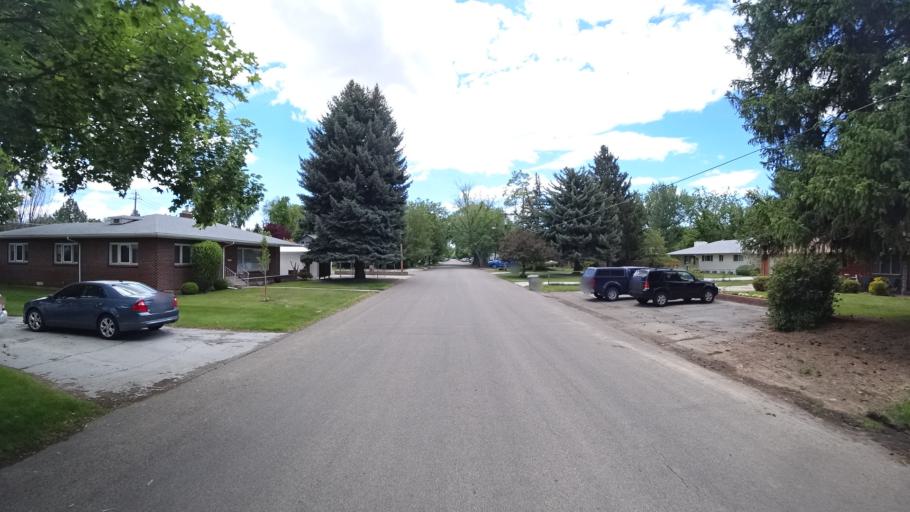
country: US
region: Idaho
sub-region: Ada County
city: Boise
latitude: 43.5892
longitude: -116.1986
